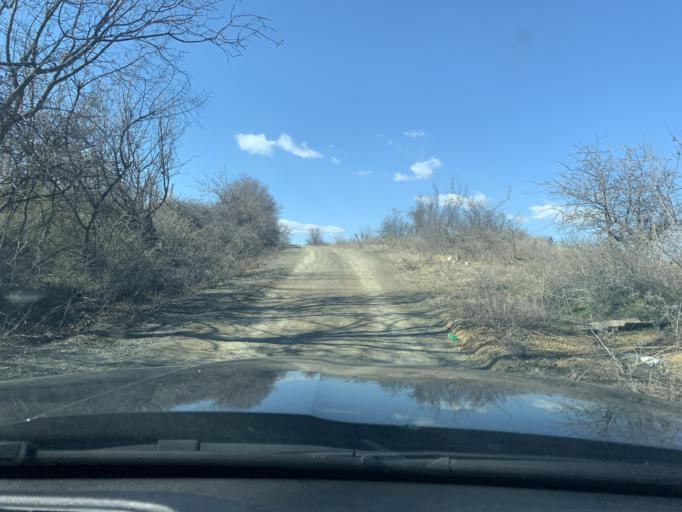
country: MK
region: Demir Kapija
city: Demir Kapija
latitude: 41.4135
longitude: 22.2226
